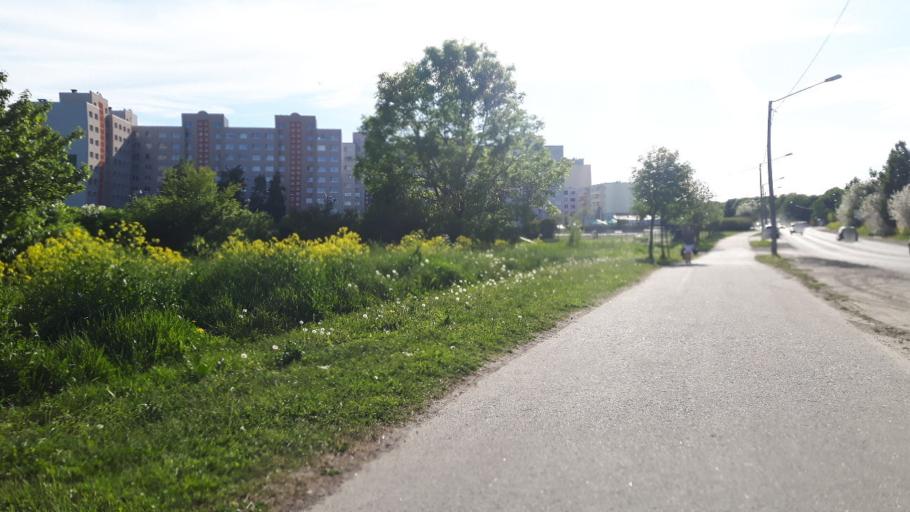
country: EE
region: Harju
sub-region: Tallinna linn
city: Kose
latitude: 59.4546
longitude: 24.8759
